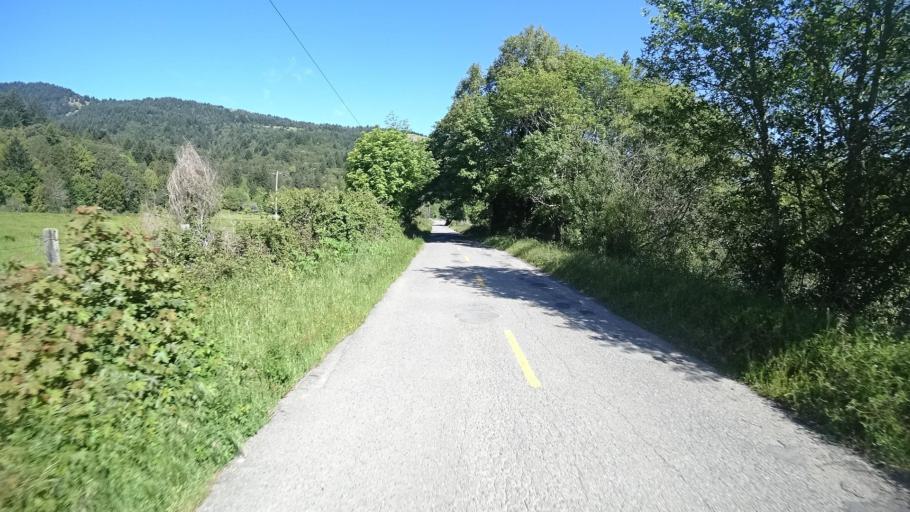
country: US
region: California
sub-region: Humboldt County
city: Rio Dell
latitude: 40.2820
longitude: -124.2497
